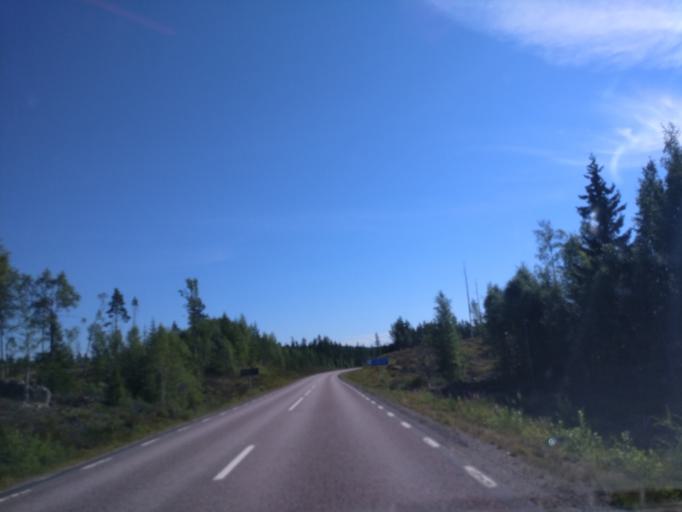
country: SE
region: Vaermland
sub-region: Filipstads Kommun
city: Lesjofors
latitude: 60.0487
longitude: 14.0093
